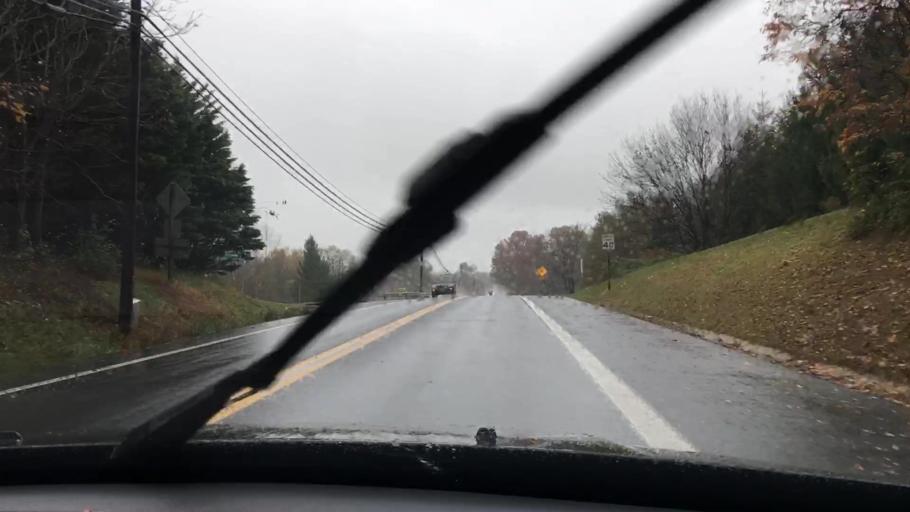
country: US
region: Maryland
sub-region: Frederick County
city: Urbana
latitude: 39.3225
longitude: -77.3630
